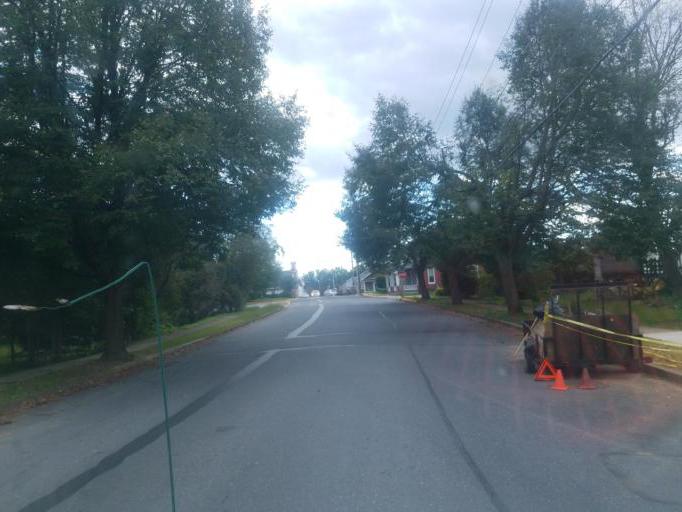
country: US
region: Pennsylvania
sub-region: Dauphin County
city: Middletown
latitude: 40.1902
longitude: -76.7339
